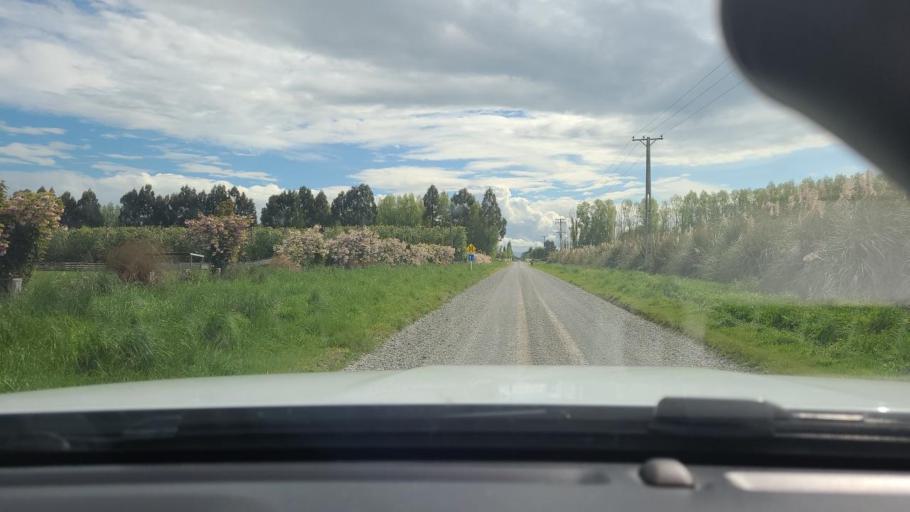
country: NZ
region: Southland
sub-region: Southland District
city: Winton
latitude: -46.1251
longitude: 168.3363
